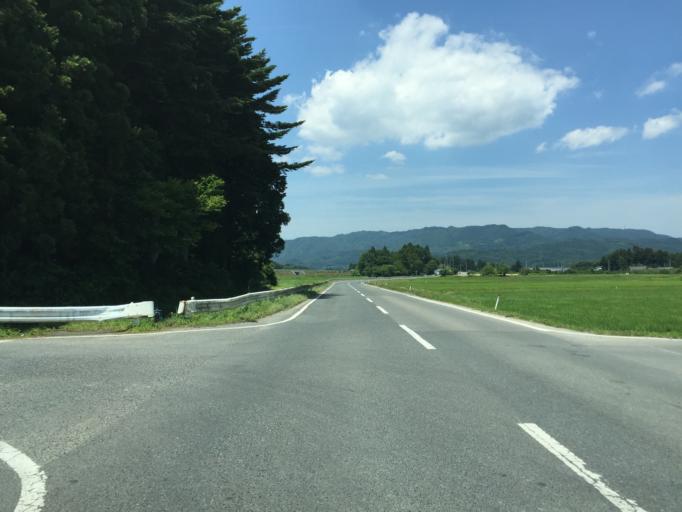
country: JP
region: Miyagi
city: Marumori
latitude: 37.7710
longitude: 140.9089
